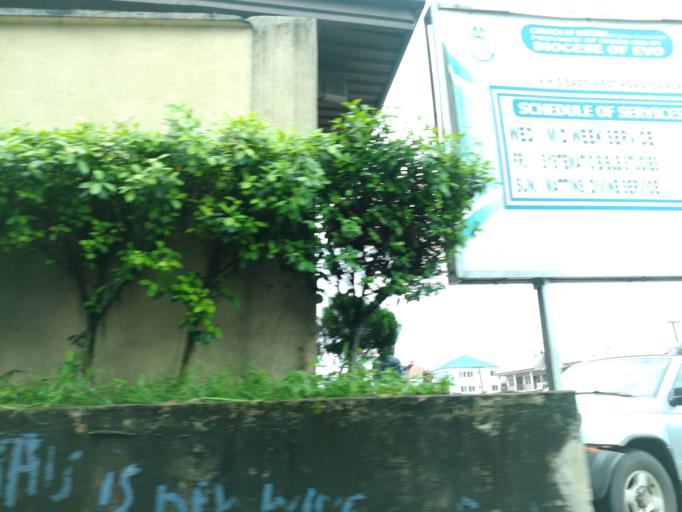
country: NG
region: Rivers
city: Port Harcourt
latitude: 4.8608
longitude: 7.0318
